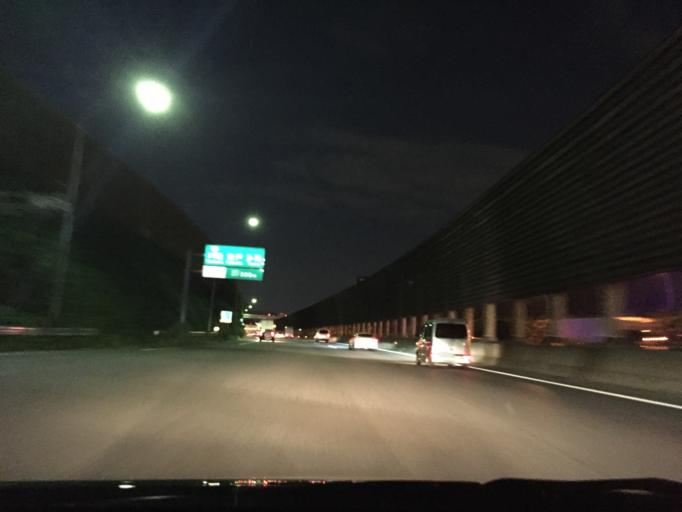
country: JP
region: Tokyo
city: Chofugaoka
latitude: 35.5931
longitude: 139.5720
